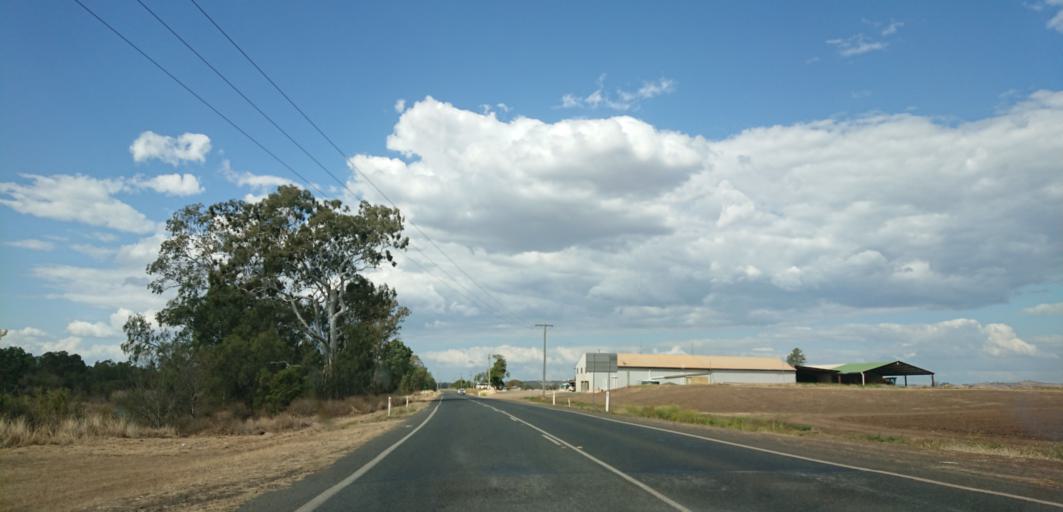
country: AU
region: Queensland
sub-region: Lockyer Valley
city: Gatton
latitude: -27.5732
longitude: 152.2320
